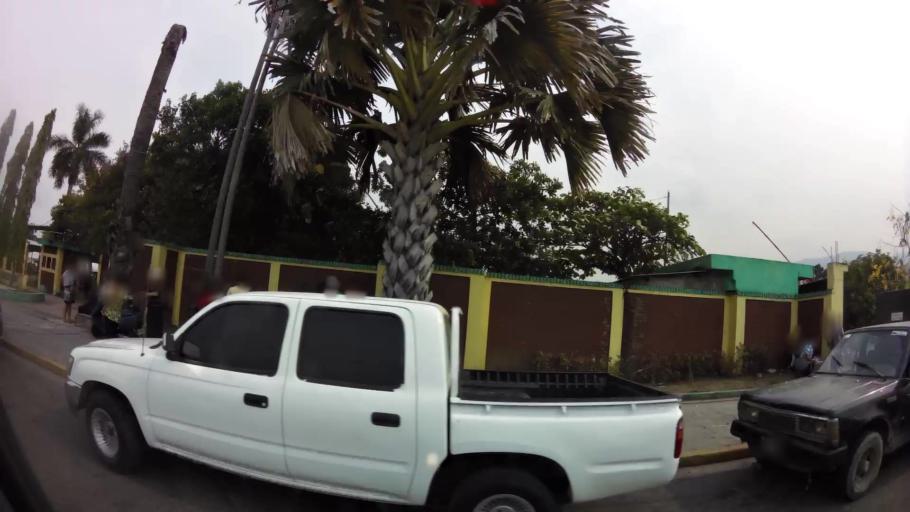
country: HN
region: Cortes
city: San Pedro Sula
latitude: 15.4951
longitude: -88.0285
